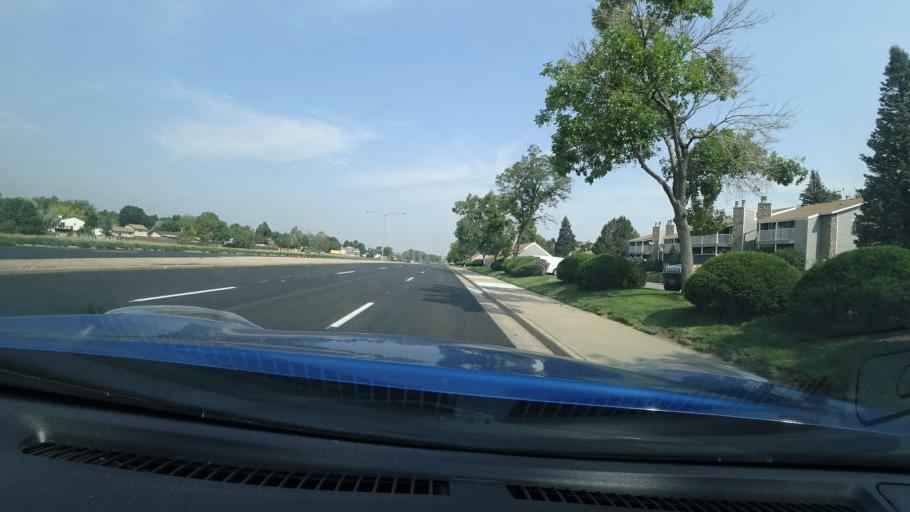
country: US
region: Colorado
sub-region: Adams County
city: Aurora
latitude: 39.7015
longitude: -104.7743
